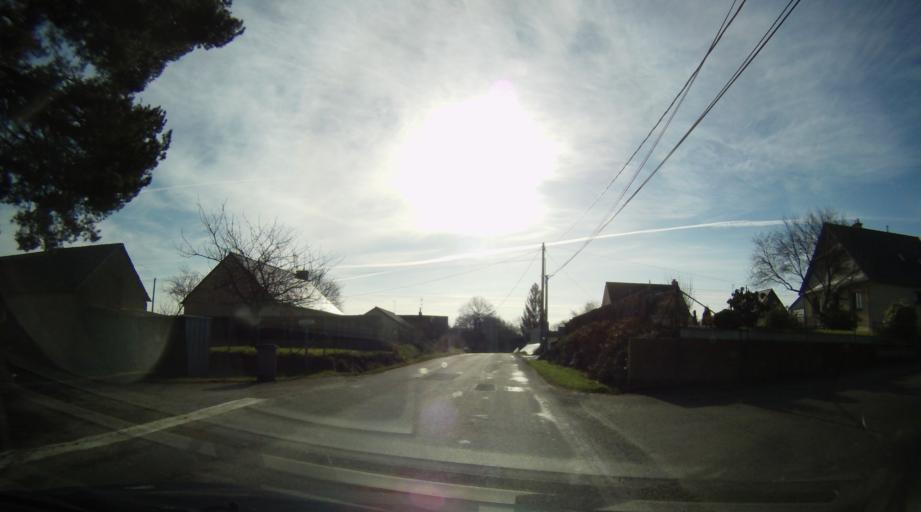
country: FR
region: Brittany
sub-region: Departement d'Ille-et-Vilaine
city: Chanteloup
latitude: 47.9709
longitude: -1.6472
